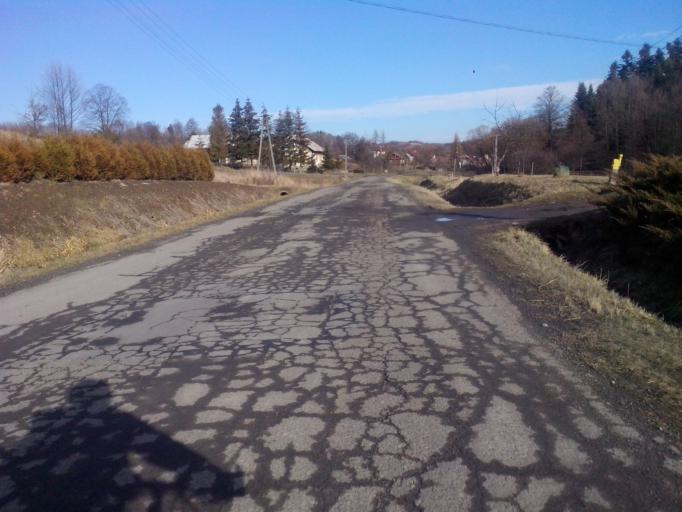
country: PL
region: Subcarpathian Voivodeship
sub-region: Powiat strzyzowski
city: Strzyzow
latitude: 49.8107
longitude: 21.8276
